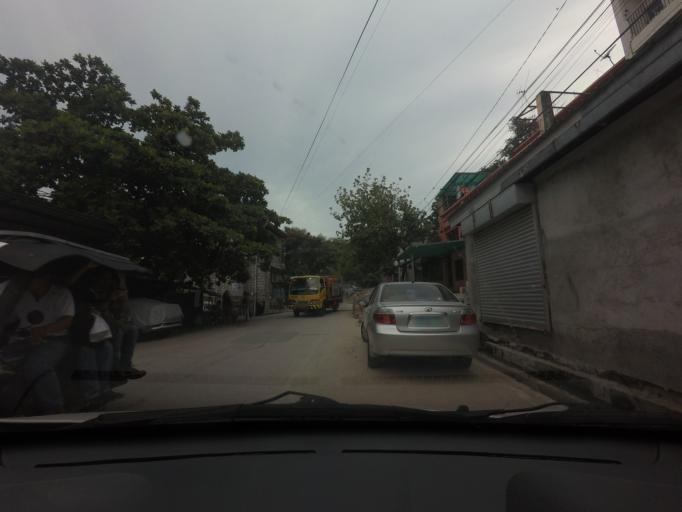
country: PH
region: Calabarzon
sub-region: Province of Rizal
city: Taguig
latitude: 14.5024
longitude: 121.0556
